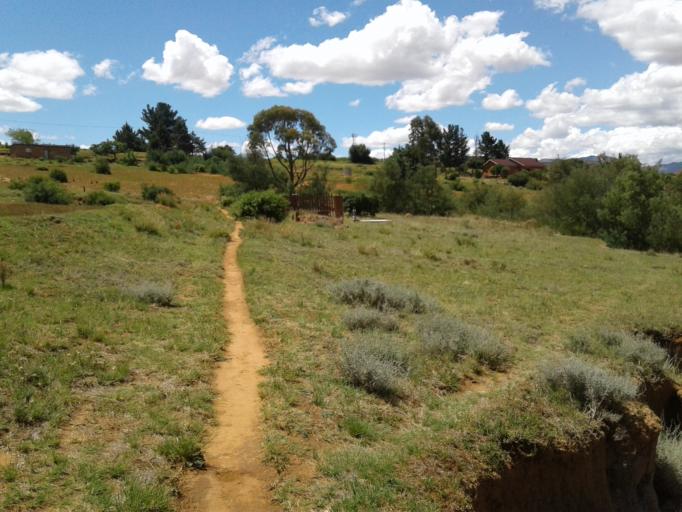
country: LS
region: Quthing
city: Quthing
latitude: -30.3803
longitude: 27.5562
